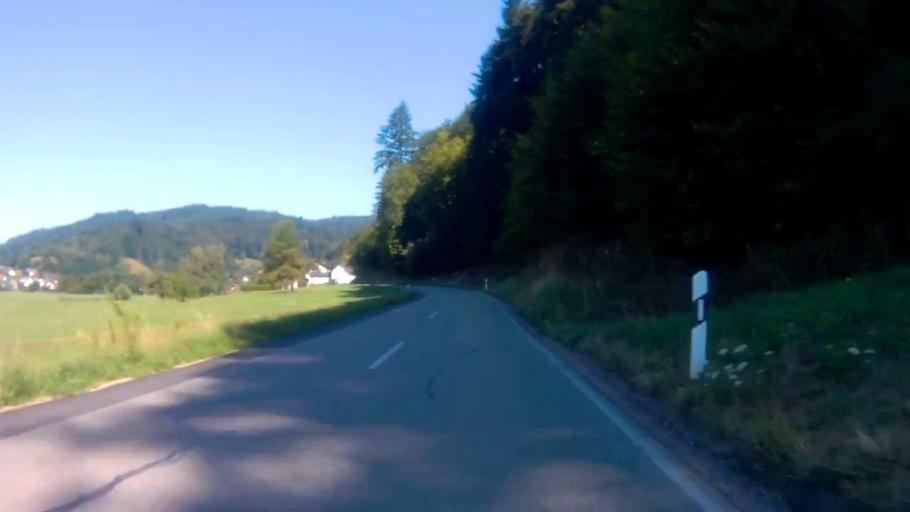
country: DE
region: Baden-Wuerttemberg
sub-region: Freiburg Region
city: Hausen
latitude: 47.6850
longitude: 7.8052
